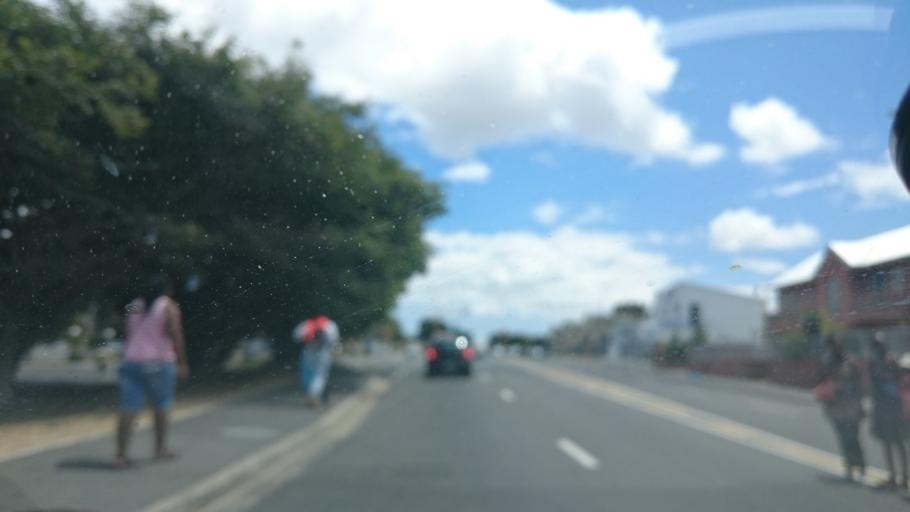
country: ZA
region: Western Cape
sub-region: City of Cape Town
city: Bergvliet
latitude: -34.0633
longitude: 18.4594
